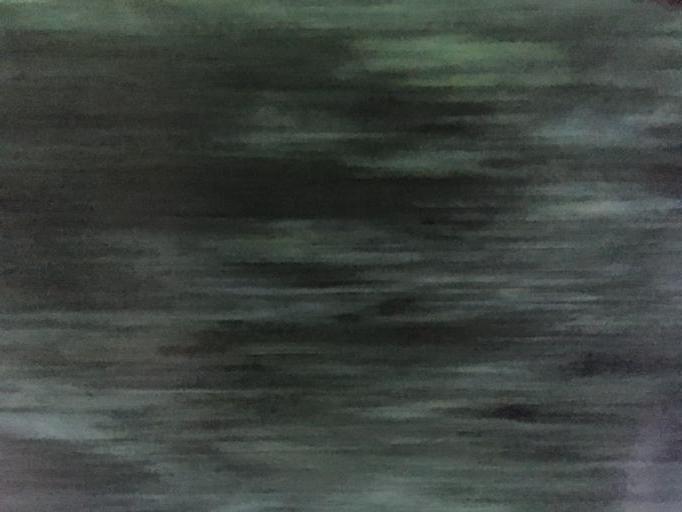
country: TW
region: Taiwan
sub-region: Chiayi
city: Jiayi Shi
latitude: 23.5034
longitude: 120.6904
